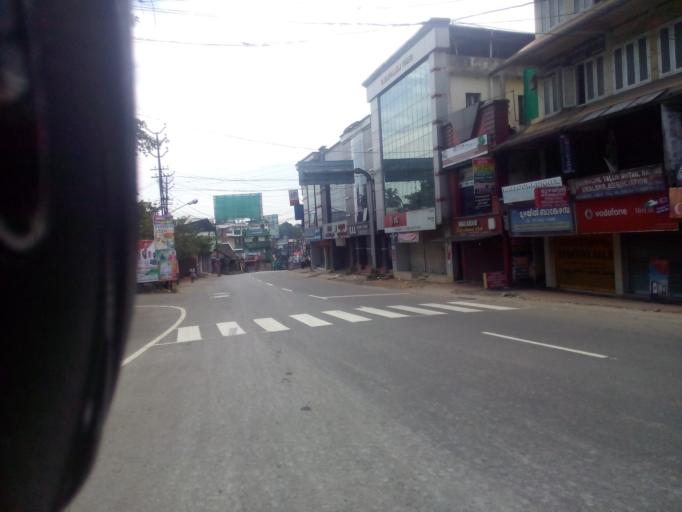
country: IN
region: Kerala
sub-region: Kottayam
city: Lalam
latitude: 9.7149
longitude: 76.6836
